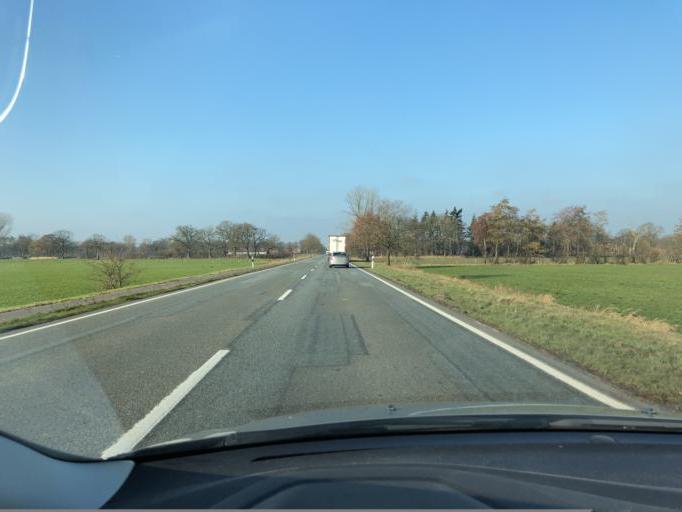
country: DE
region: Lower Saxony
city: Apen
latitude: 53.3007
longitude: 7.7980
